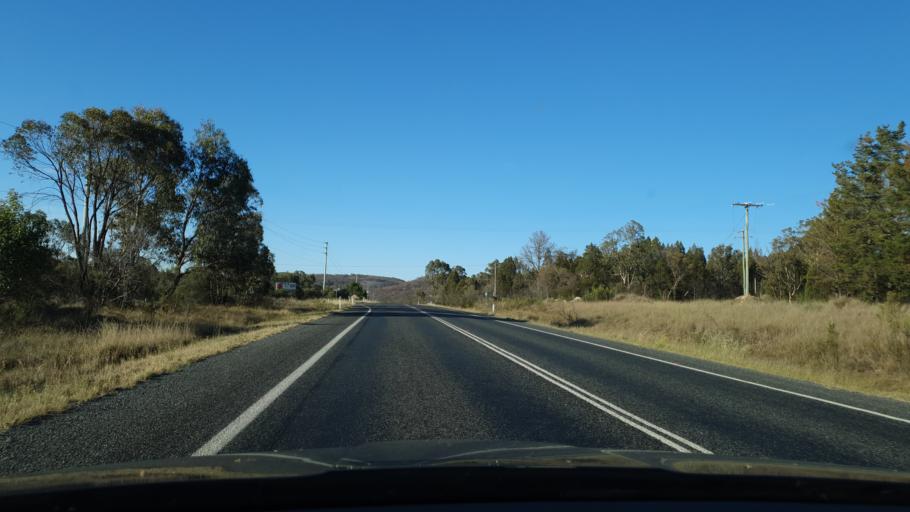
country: AU
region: Queensland
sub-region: Southern Downs
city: Stanthorpe
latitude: -28.6629
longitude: 151.9160
